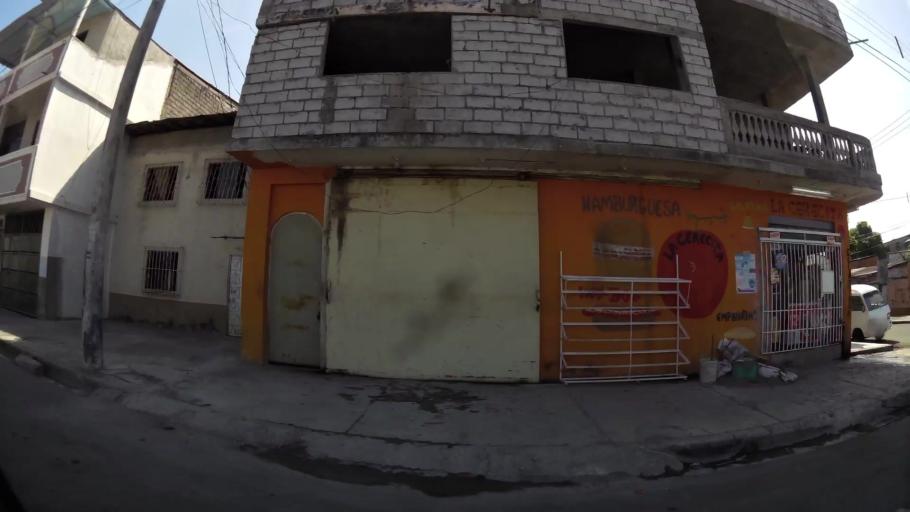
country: EC
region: Guayas
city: Guayaquil
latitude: -2.2203
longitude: -79.8998
